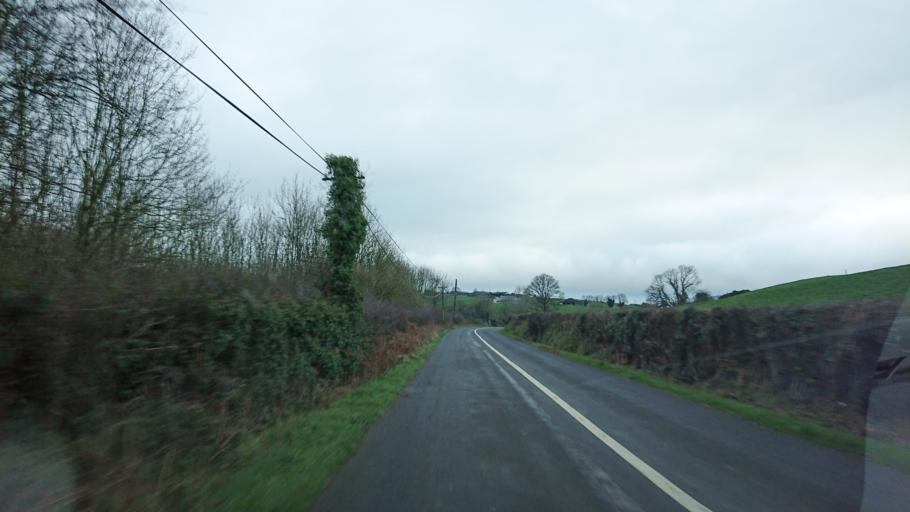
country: IE
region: Munster
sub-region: Waterford
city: Portlaw
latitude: 52.2715
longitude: -7.3922
